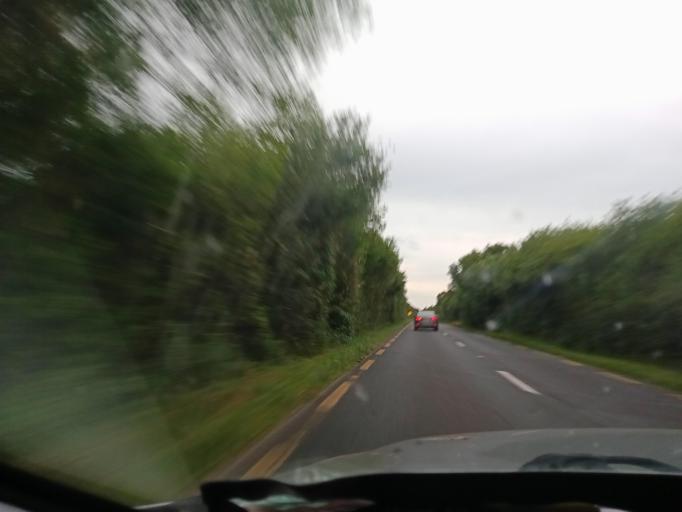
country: IE
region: Leinster
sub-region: Laois
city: Mountmellick
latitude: 53.0716
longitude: -7.3285
